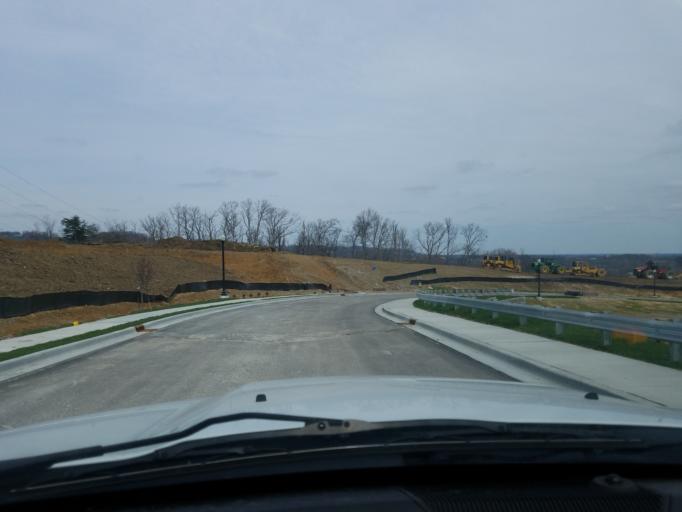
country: US
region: Indiana
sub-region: Floyd County
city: New Albany
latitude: 38.3063
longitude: -85.8470
